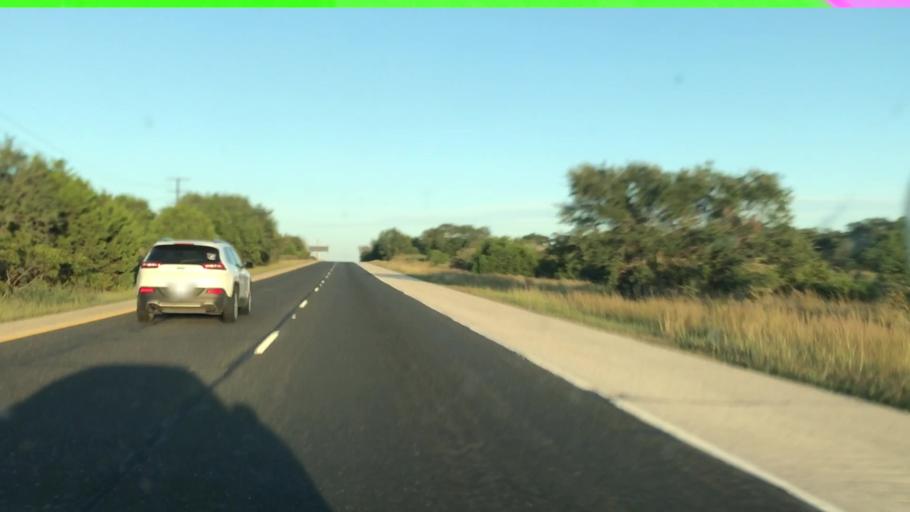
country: US
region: Texas
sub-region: Kerr County
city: Kerrville
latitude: 30.0677
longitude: -99.0642
